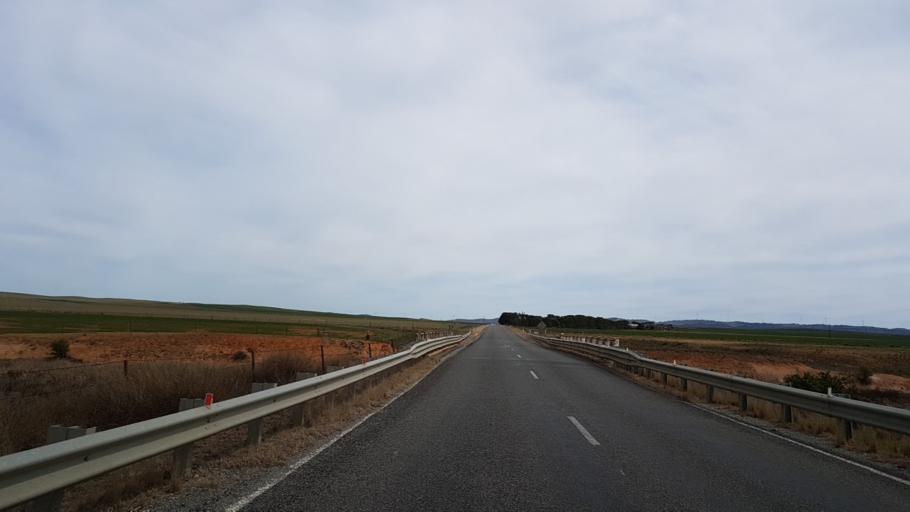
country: AU
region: South Australia
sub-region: Peterborough
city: Peterborough
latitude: -33.0166
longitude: 138.6955
